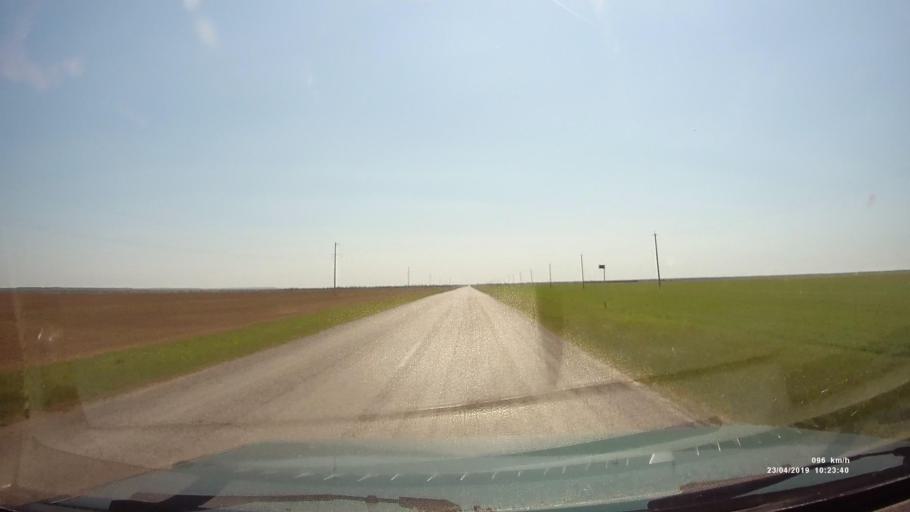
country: RU
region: Rostov
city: Sovetskoye
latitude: 46.6456
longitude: 42.4284
